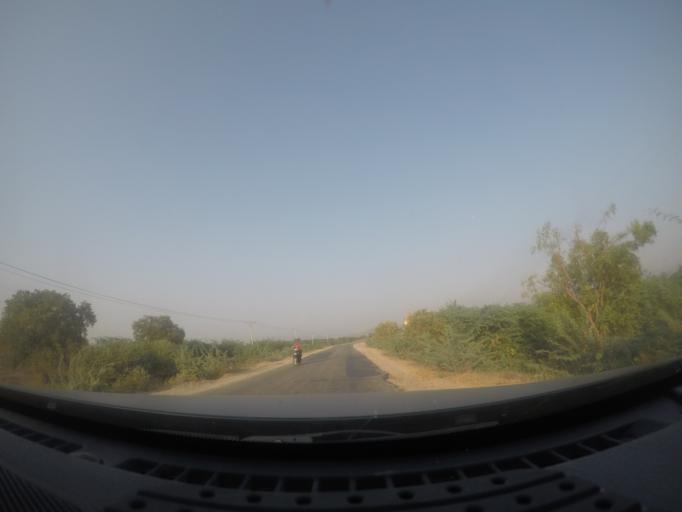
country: MM
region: Mandalay
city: Yamethin
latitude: 20.6812
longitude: 96.1487
